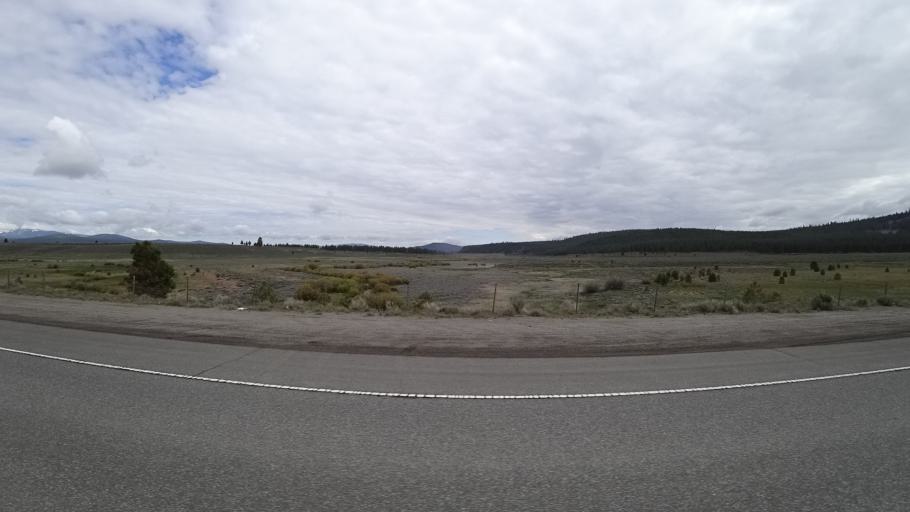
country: US
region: California
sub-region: Nevada County
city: Truckee
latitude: 39.3025
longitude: -120.1202
